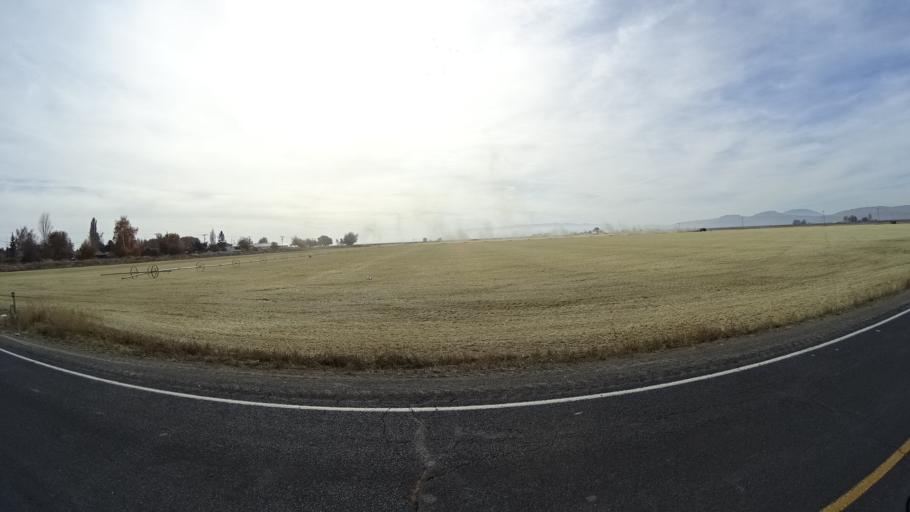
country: US
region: California
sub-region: Siskiyou County
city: Tulelake
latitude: 41.9537
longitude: -121.4828
